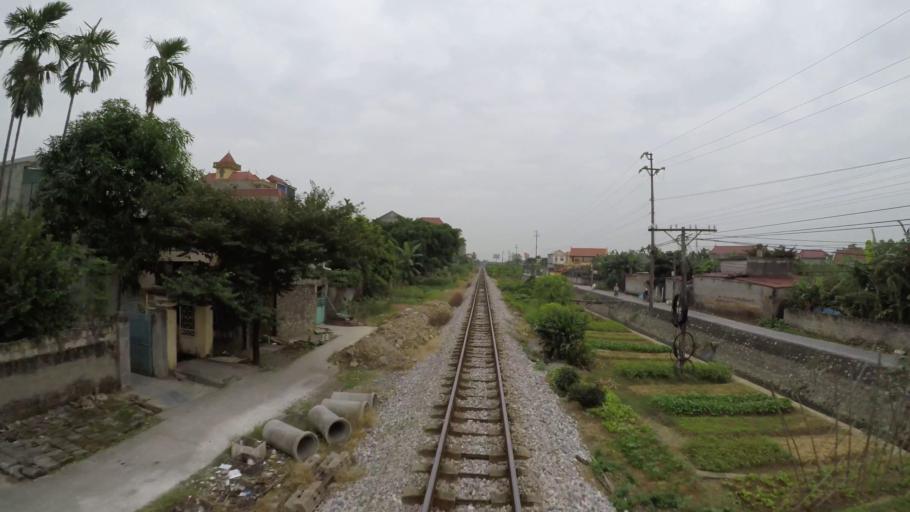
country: VN
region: Hai Phong
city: An Duong
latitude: 20.9151
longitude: 106.5651
